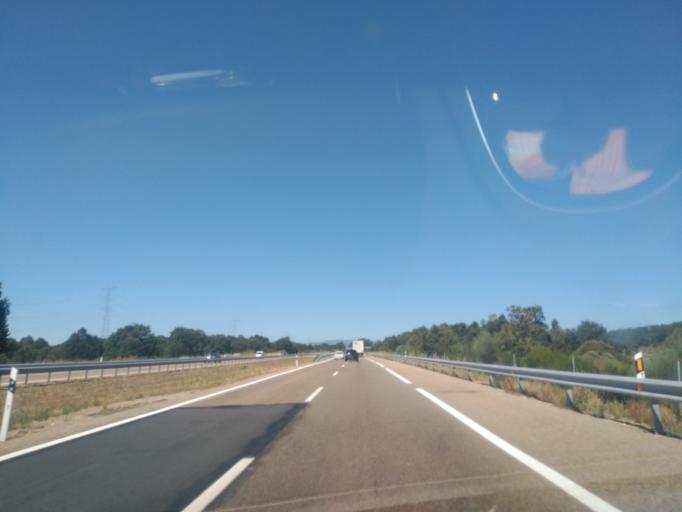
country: ES
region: Castille and Leon
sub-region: Provincia de Zamora
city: Cernadilla
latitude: 42.0388
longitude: -6.4498
